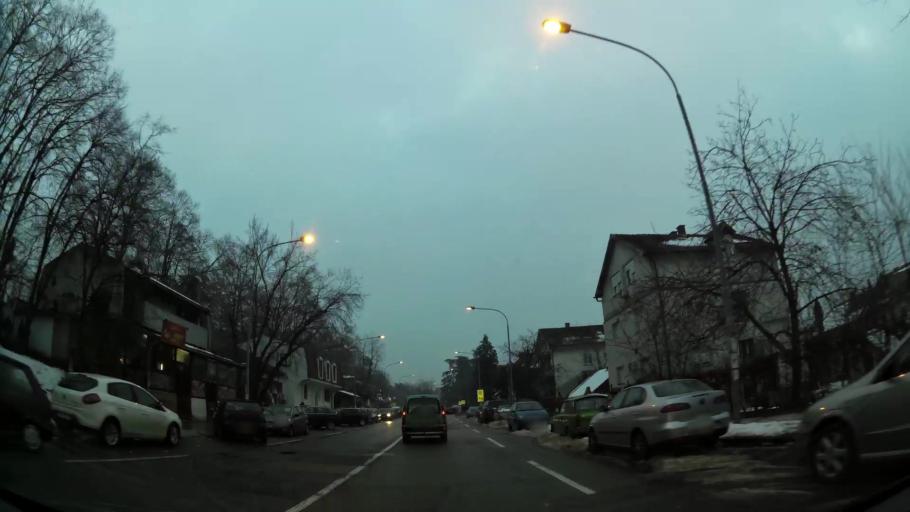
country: RS
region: Central Serbia
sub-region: Belgrade
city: Vozdovac
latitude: 44.7726
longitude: 20.4929
